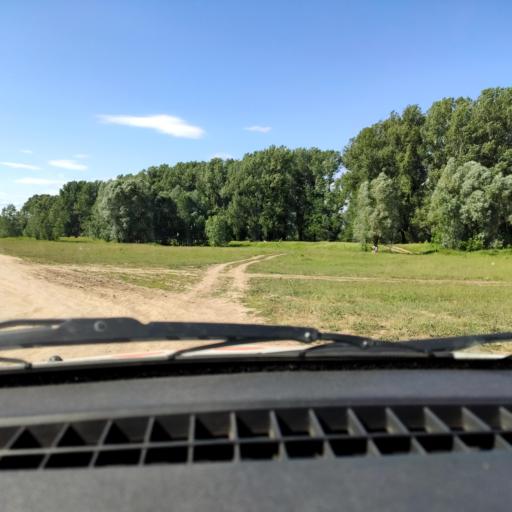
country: RU
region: Bashkortostan
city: Iglino
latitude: 54.7983
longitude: 56.2286
